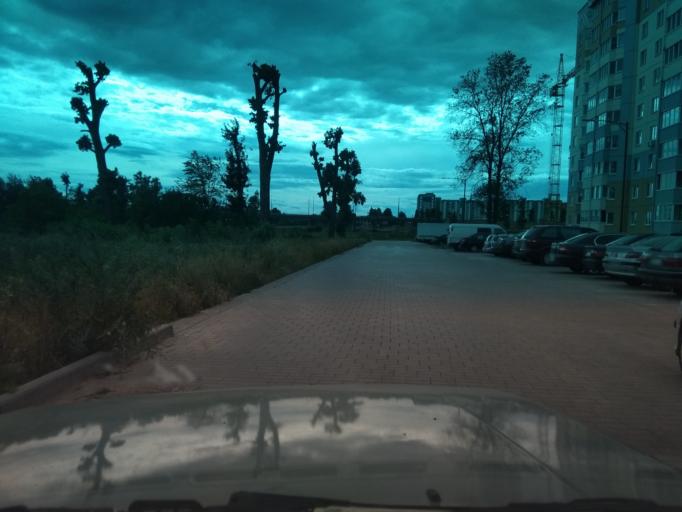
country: BY
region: Mogilev
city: Mahilyow
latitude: 53.9218
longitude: 30.3542
